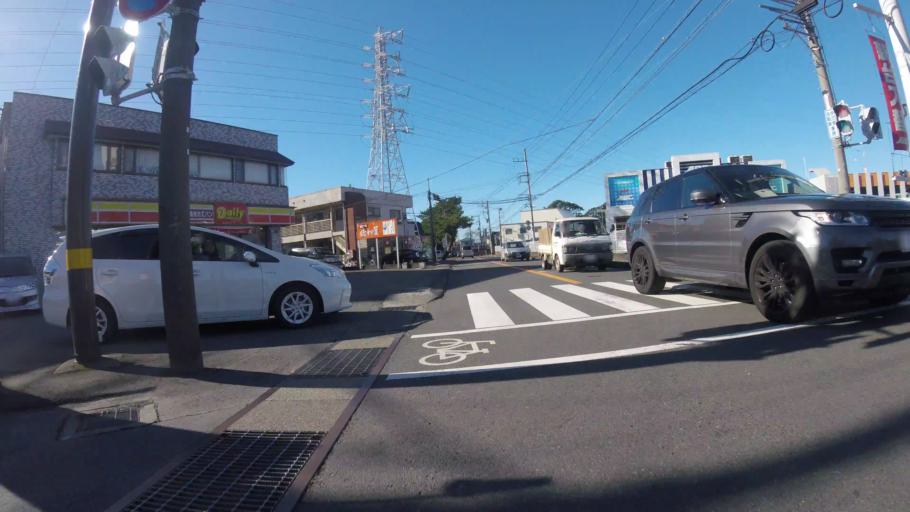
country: JP
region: Shizuoka
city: Numazu
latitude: 35.1063
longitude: 138.8915
